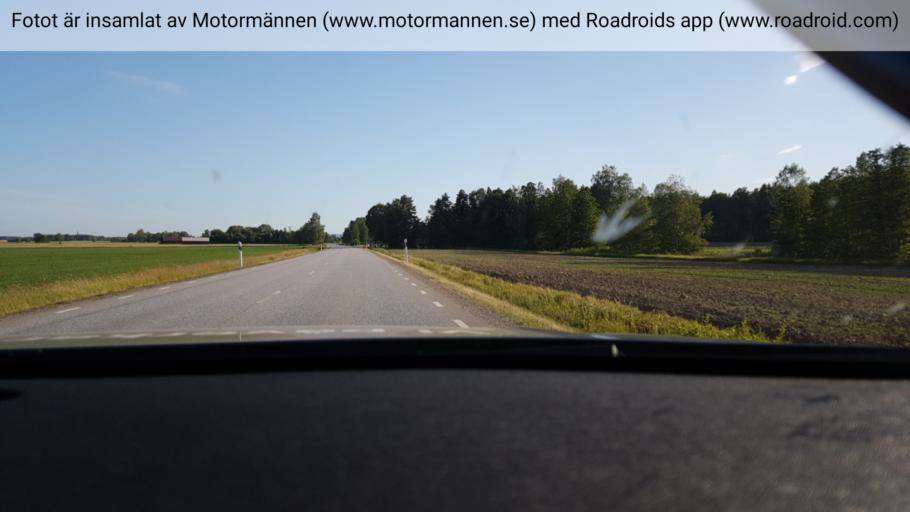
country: SE
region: Vaestra Goetaland
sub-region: Toreboda Kommun
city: Toereboda
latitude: 58.6321
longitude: 14.0206
